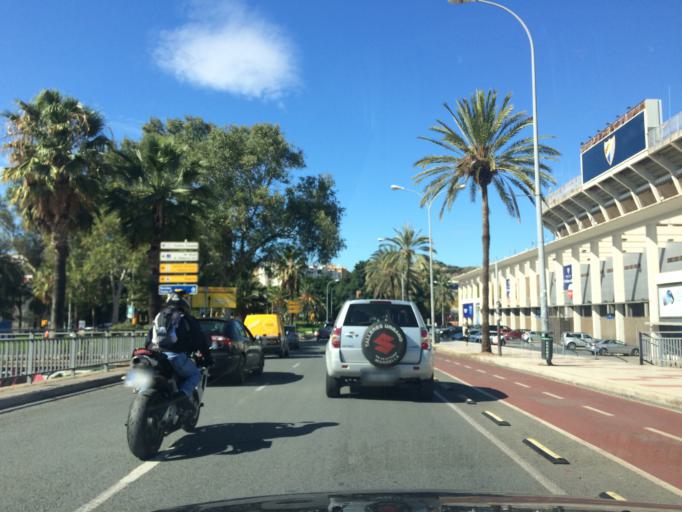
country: ES
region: Andalusia
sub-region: Provincia de Malaga
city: Malaga
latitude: 36.7330
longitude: -4.4258
